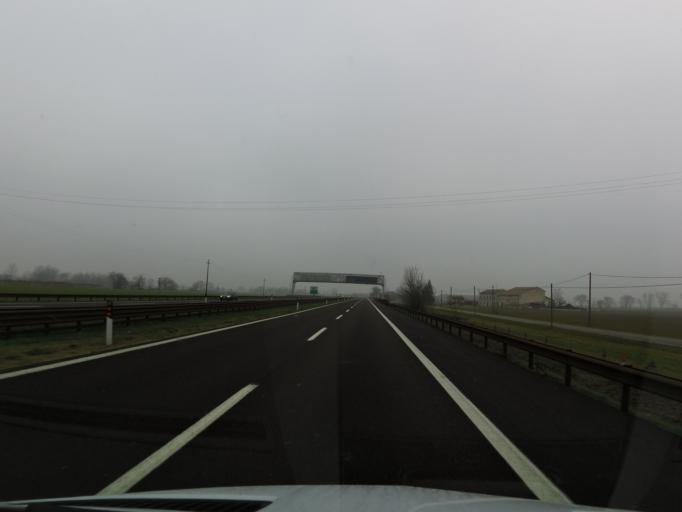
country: IT
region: Lombardy
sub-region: Provincia di Mantova
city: Bondeno
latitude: 44.9602
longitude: 10.8611
